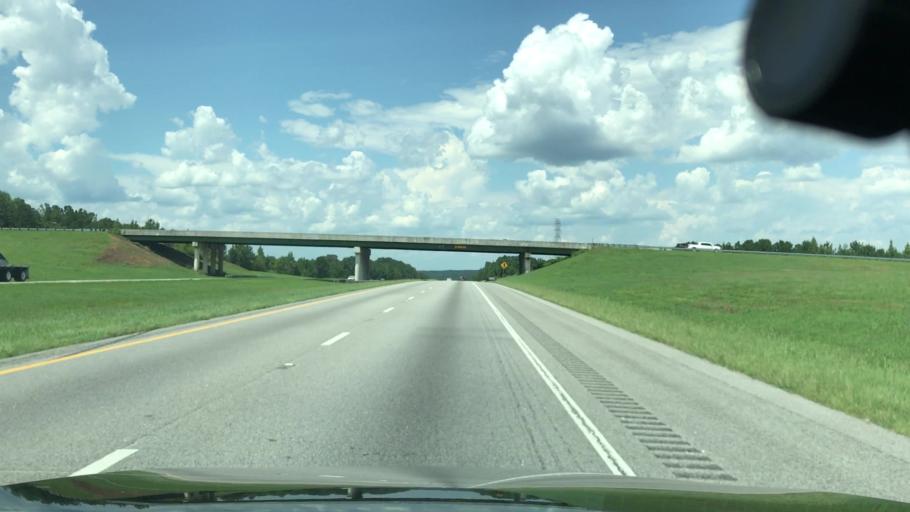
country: US
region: South Carolina
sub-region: Chester County
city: Great Falls
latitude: 34.6087
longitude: -81.0189
